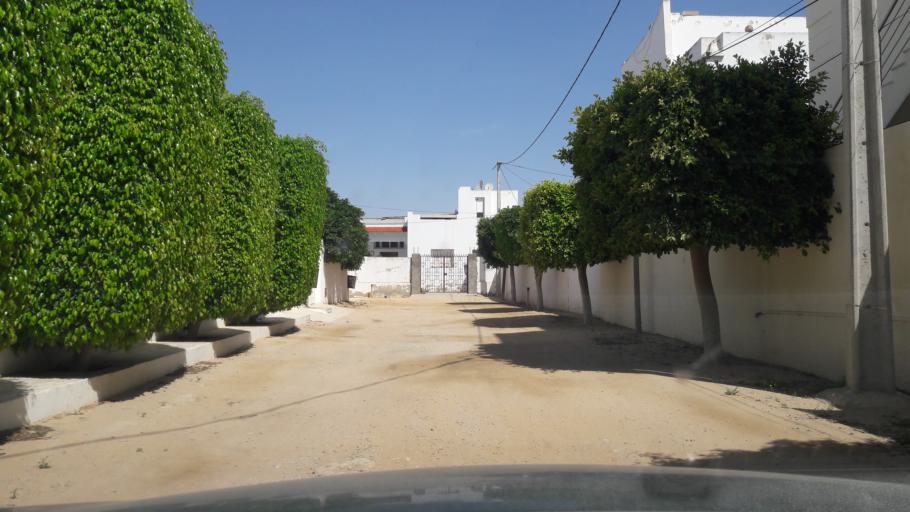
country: TN
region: Safaqis
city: Al Qarmadah
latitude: 34.7885
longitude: 10.7547
